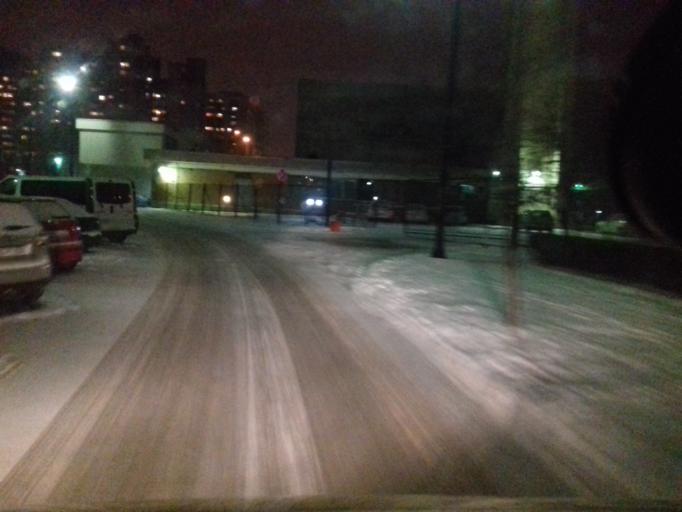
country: BA
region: Federation of Bosnia and Herzegovina
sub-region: Kanton Sarajevo
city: Sarajevo
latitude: 43.8405
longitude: 18.3474
